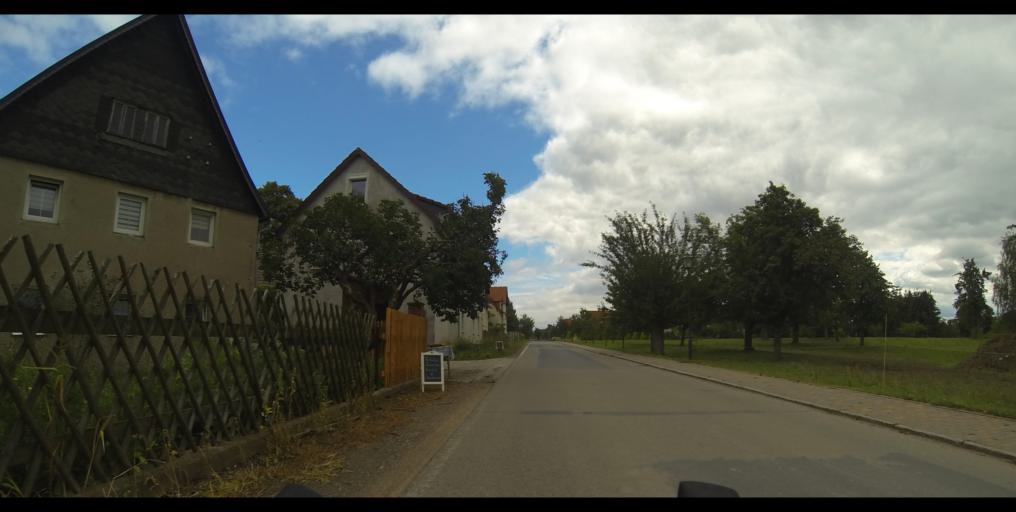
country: DE
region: Saxony
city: Wilsdruff
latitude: 51.0521
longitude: 13.5704
